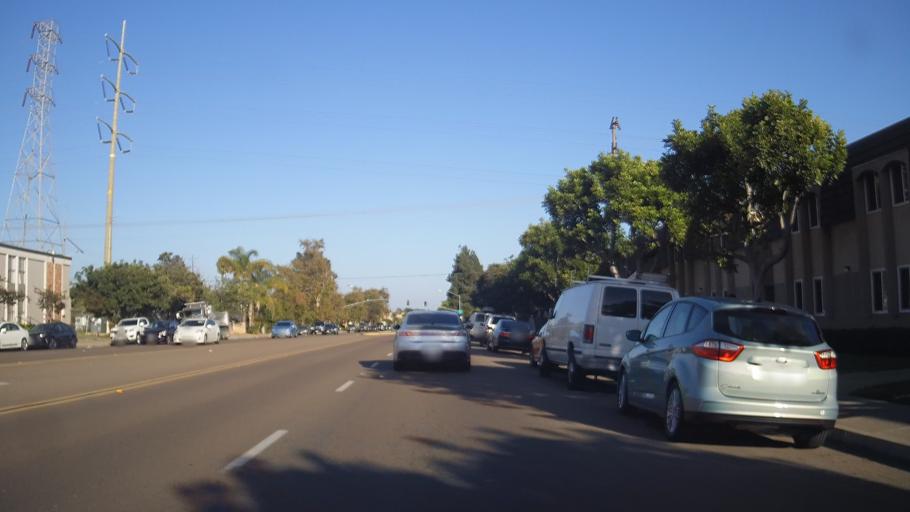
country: US
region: California
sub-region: San Diego County
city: La Jolla
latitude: 32.8344
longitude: -117.1849
